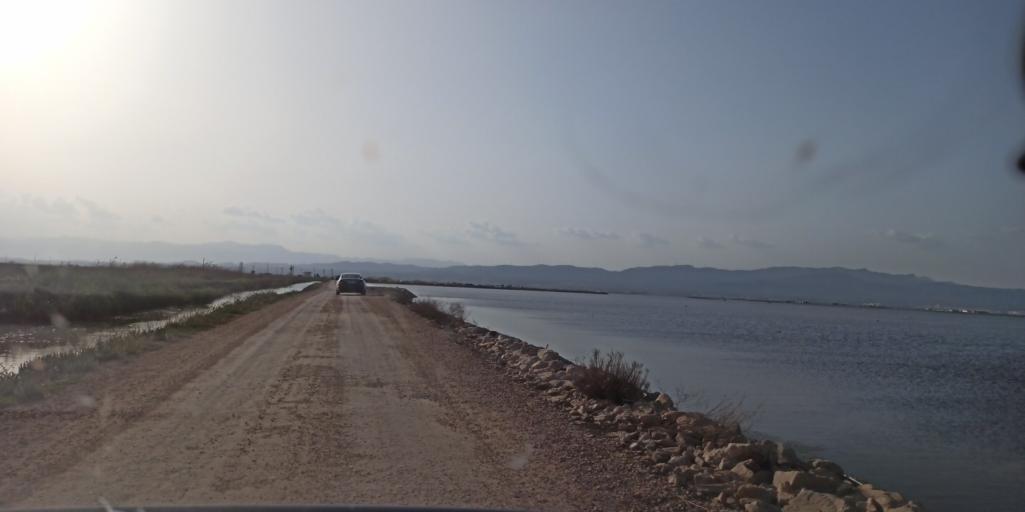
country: ES
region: Catalonia
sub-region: Provincia de Tarragona
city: Deltebre
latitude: 40.7650
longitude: 0.7461
